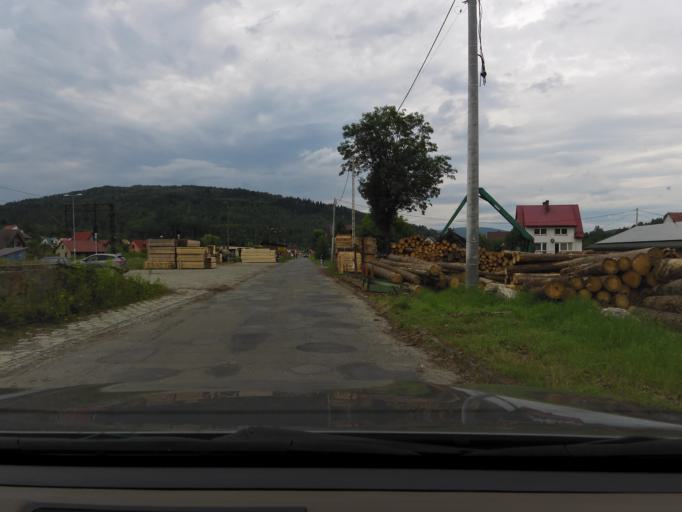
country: PL
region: Silesian Voivodeship
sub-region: Powiat zywiecki
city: Rajcza
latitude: 49.5176
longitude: 19.1122
